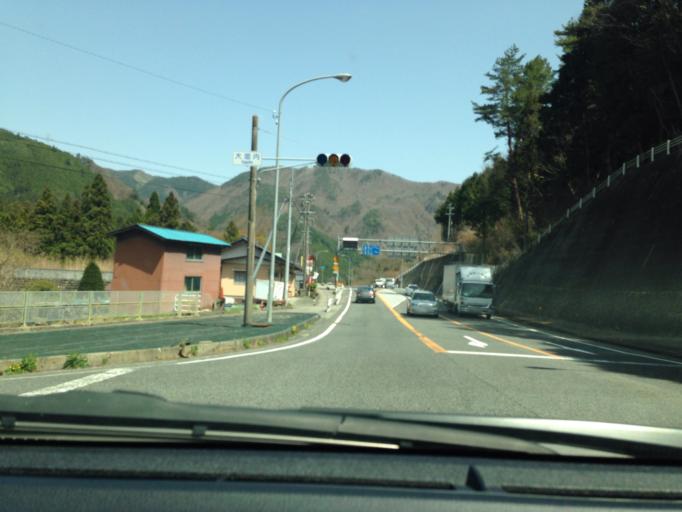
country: JP
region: Gifu
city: Takayama
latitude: 35.9621
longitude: 137.2606
